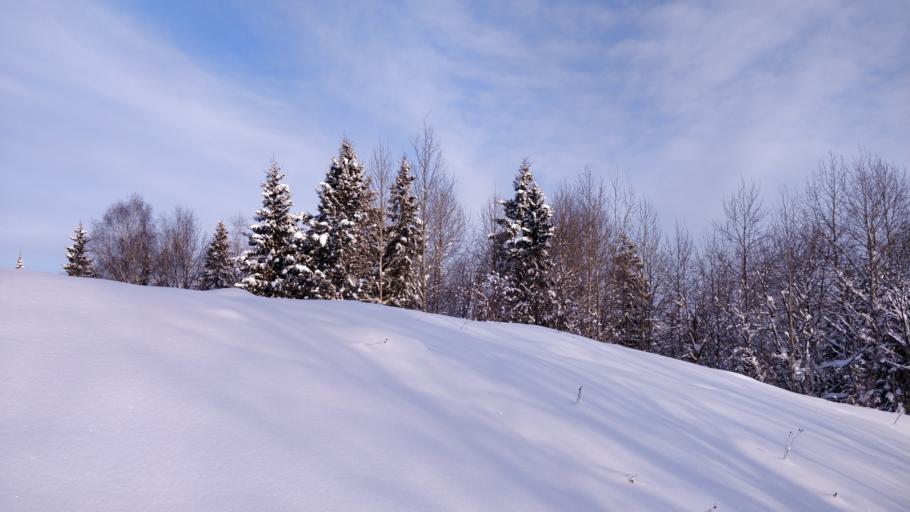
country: RU
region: Perm
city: Verkhnechusovskiye Gorodki
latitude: 58.2124
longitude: 57.0704
